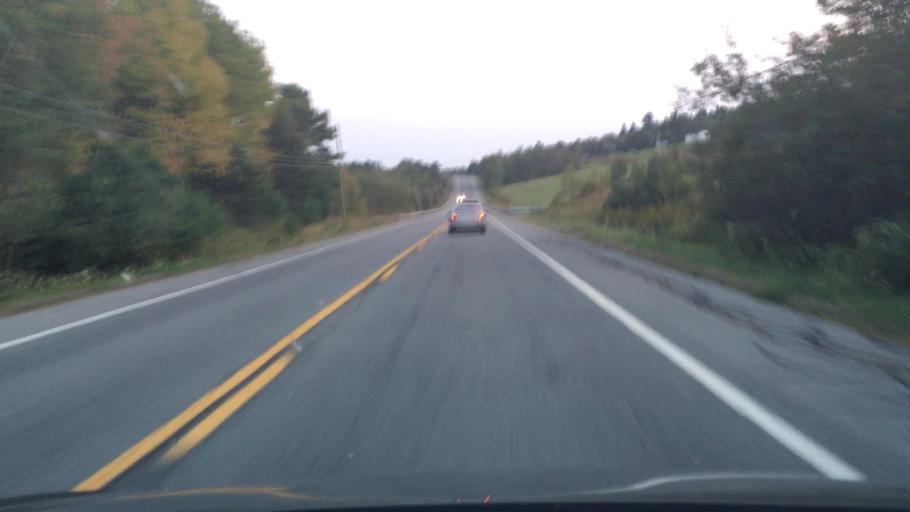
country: US
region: Maine
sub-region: Waldo County
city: Stockton Springs
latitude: 44.5307
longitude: -68.8614
